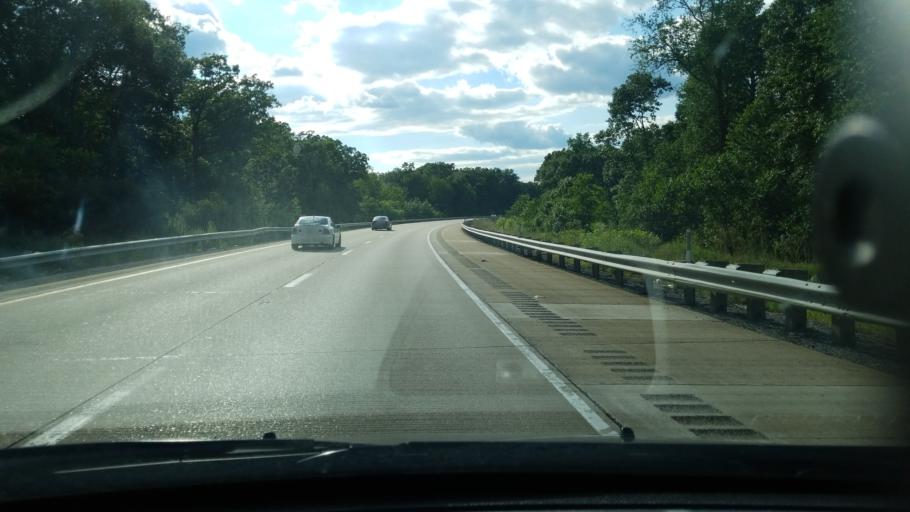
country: US
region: Pennsylvania
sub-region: Northumberland County
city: Milton
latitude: 40.9935
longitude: -76.7393
